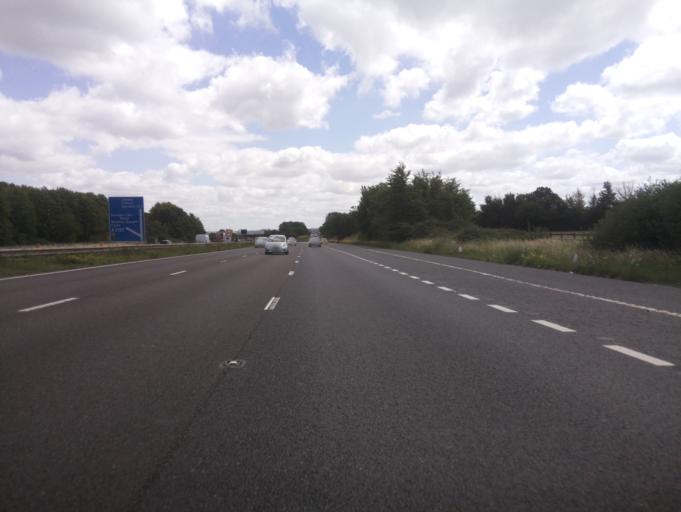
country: GB
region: England
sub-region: Wiltshire
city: Lydiard Tregoze
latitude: 51.5484
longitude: -1.8622
